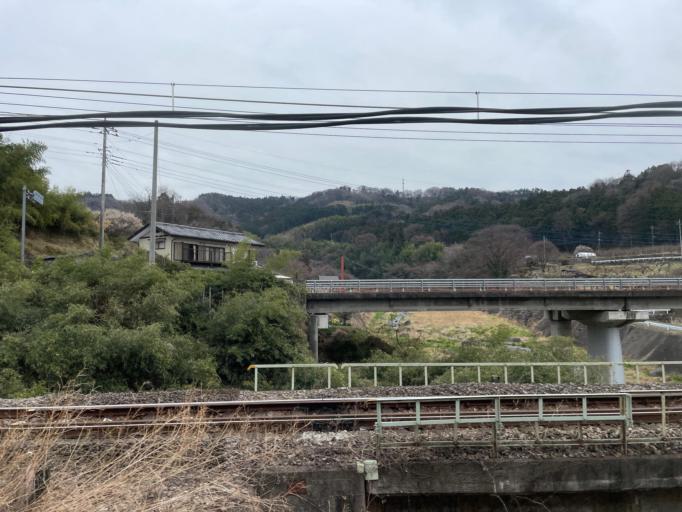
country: JP
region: Gunma
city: Numata
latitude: 36.5555
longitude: 139.0443
